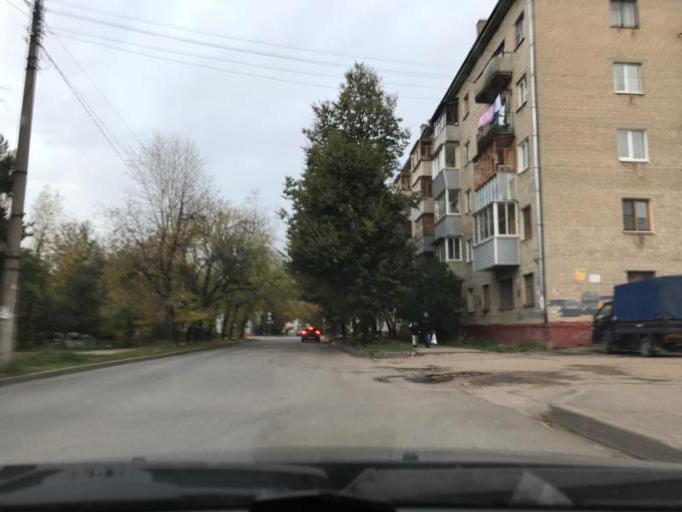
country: RU
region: Kaluga
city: Kaluga
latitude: 54.5342
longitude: 36.2570
